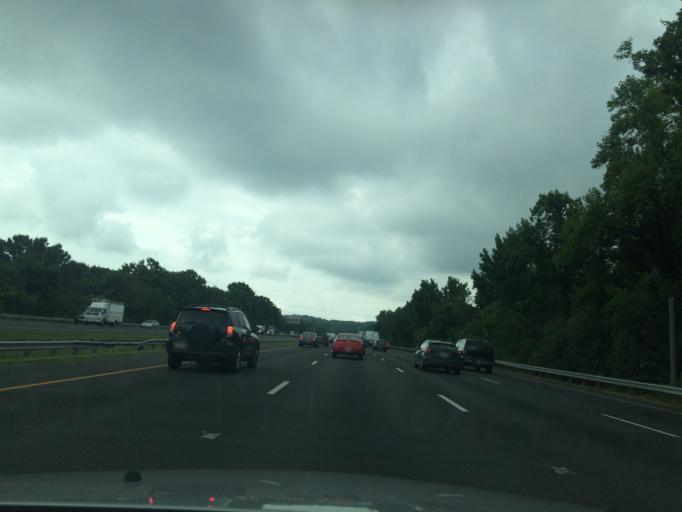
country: US
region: Maryland
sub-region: Prince George's County
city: Largo
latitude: 38.8807
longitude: -76.8440
